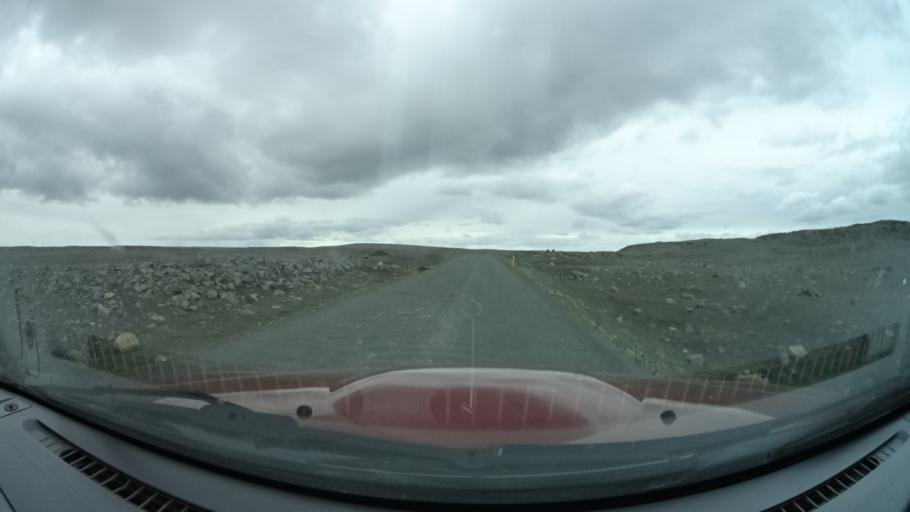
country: IS
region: Northeast
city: Husavik
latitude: 65.8163
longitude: -16.3529
